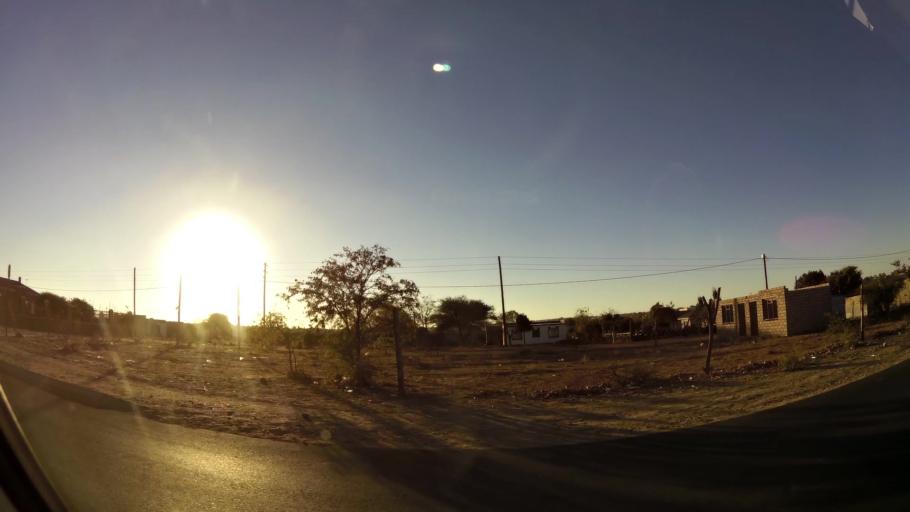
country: ZA
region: Limpopo
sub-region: Capricorn District Municipality
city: Polokwane
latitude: -23.8315
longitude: 29.3717
